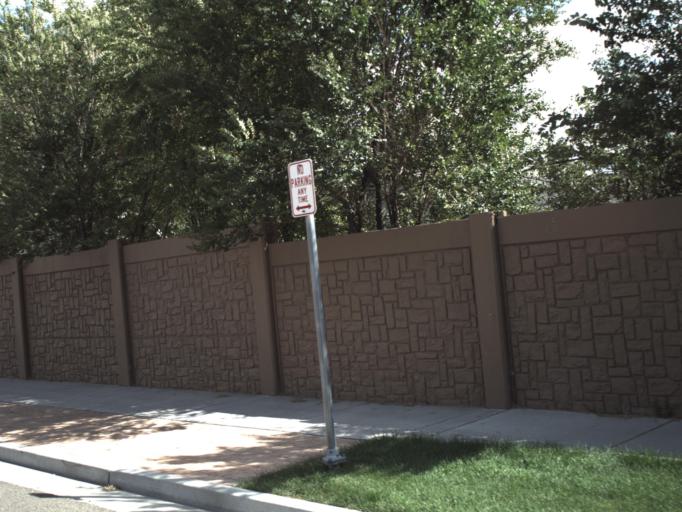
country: US
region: Utah
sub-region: Utah County
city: Orem
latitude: 40.3119
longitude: -111.6882
